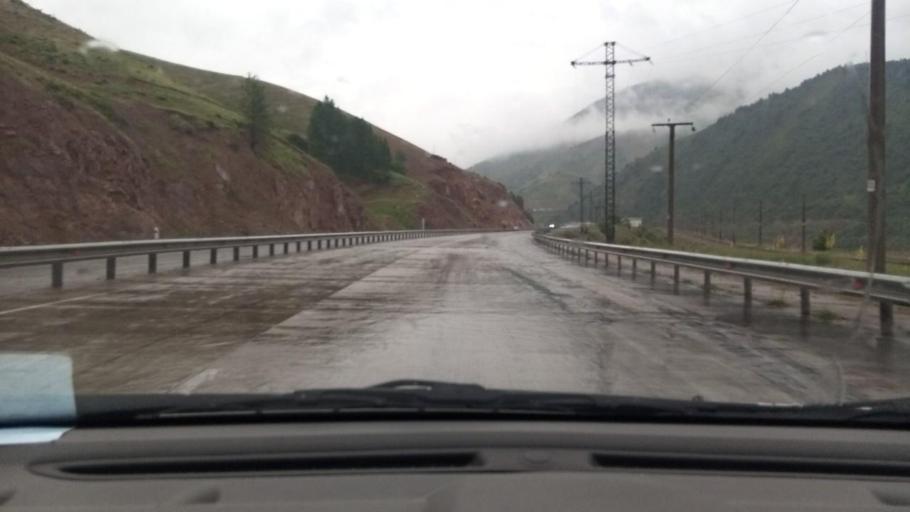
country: UZ
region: Toshkent
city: Angren
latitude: 41.1509
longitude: 70.4254
